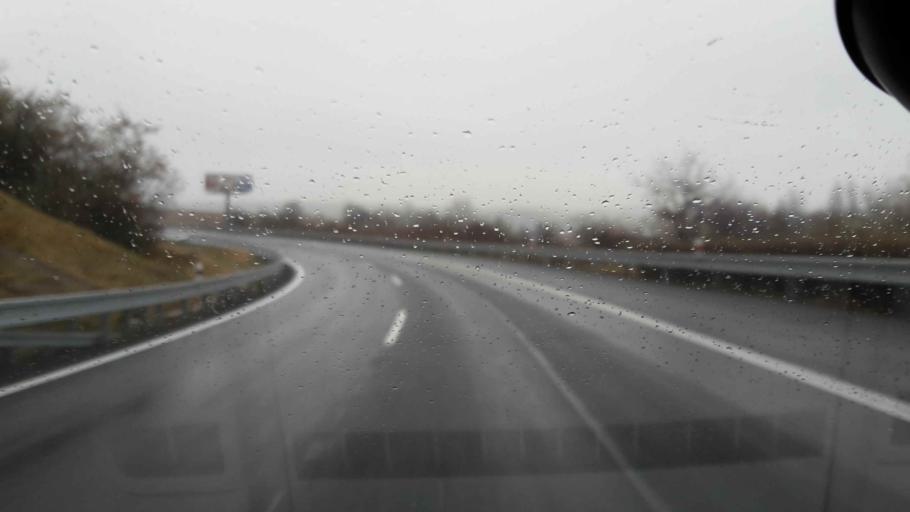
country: CZ
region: South Moravian
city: Podoli
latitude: 49.1824
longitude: 16.7145
